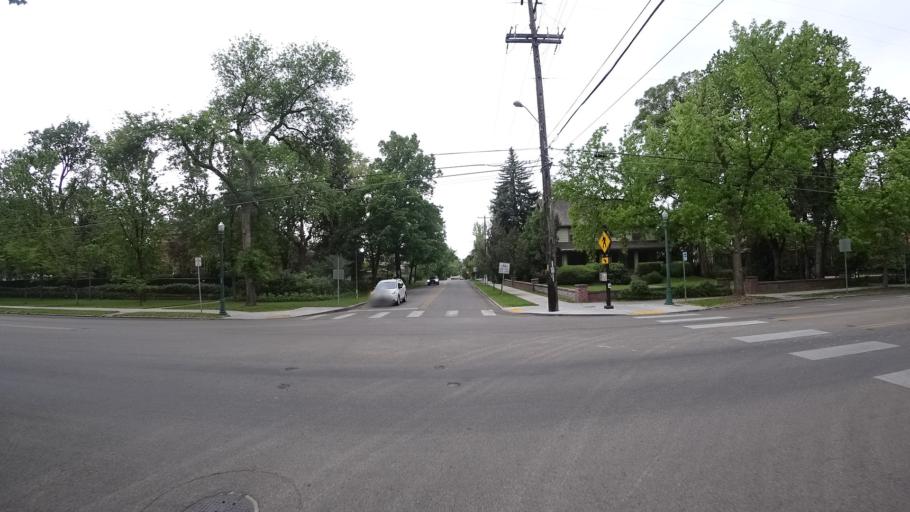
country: US
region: Idaho
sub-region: Ada County
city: Boise
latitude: 43.6072
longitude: -116.1825
